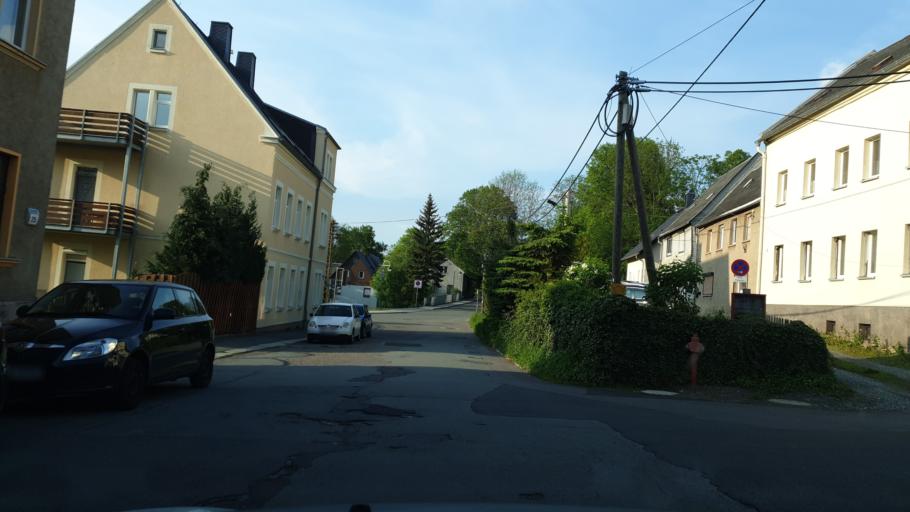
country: DE
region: Saxony
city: Stollberg
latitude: 50.7132
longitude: 12.7864
